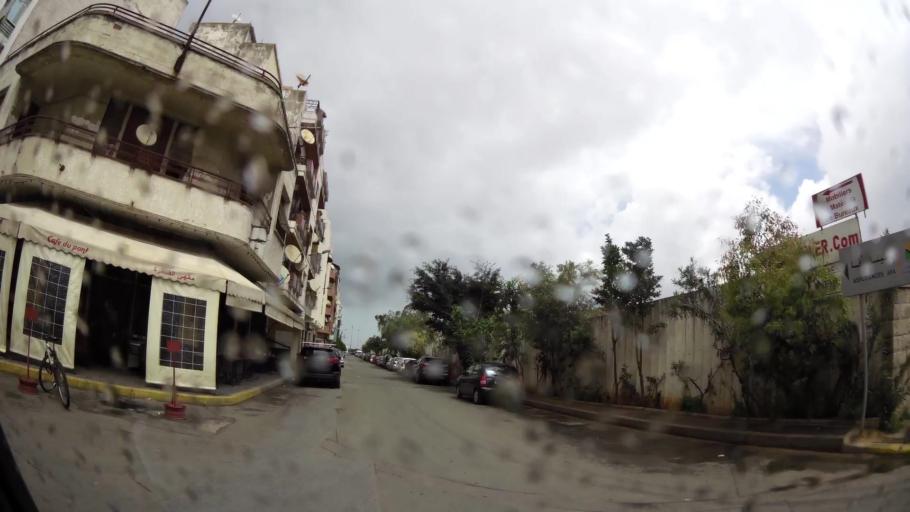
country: MA
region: Grand Casablanca
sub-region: Casablanca
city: Casablanca
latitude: 33.5825
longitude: -7.5984
